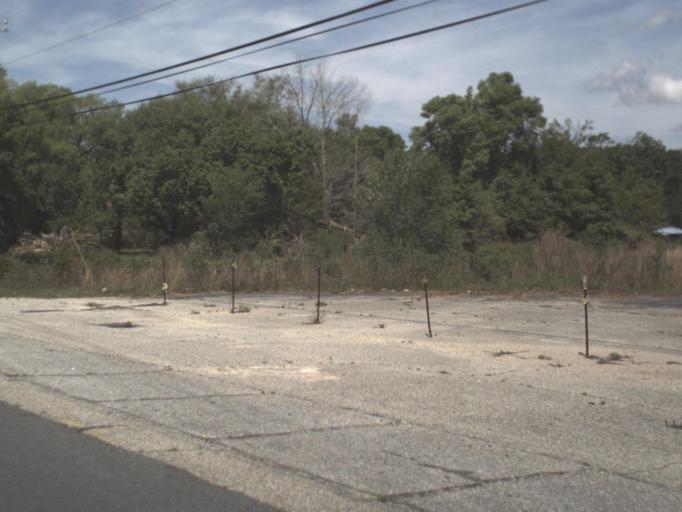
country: US
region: Florida
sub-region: Santa Rosa County
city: Pace
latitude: 30.6036
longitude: -87.1232
